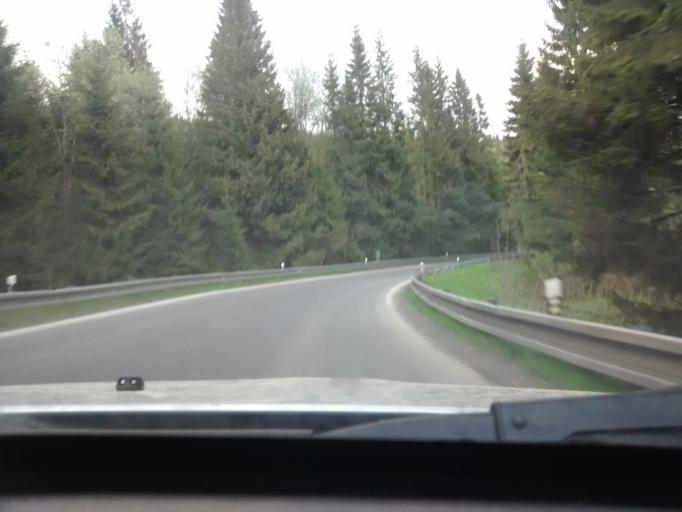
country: SK
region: Presovsky
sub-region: Okres Poprad
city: Zdiar
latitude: 49.2802
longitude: 20.2078
